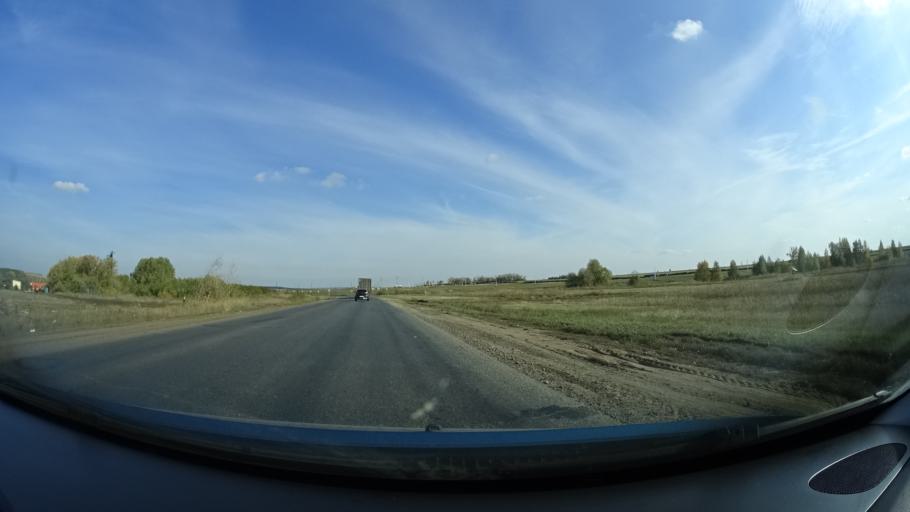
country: RU
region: Bashkortostan
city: Buzdyak
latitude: 54.6262
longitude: 54.4474
